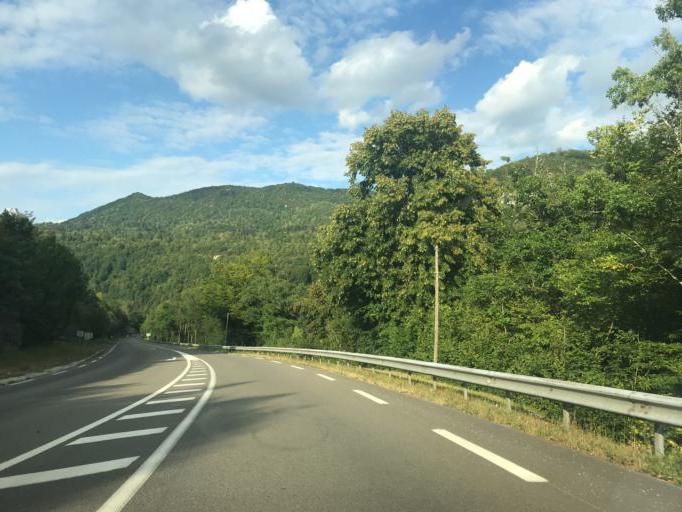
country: FR
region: Franche-Comte
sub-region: Departement du Jura
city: Saint-Lupicin
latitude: 46.3859
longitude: 5.7977
